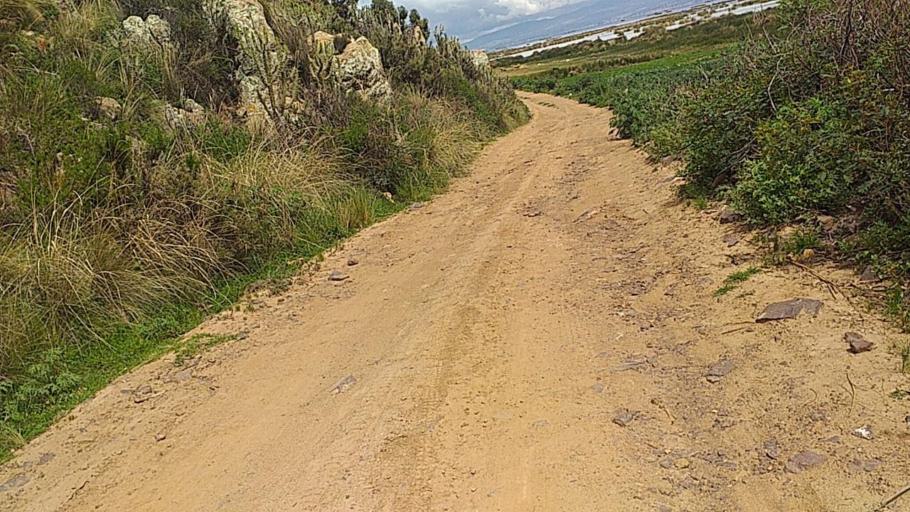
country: BO
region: La Paz
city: Batallas
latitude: -16.3245
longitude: -68.6467
